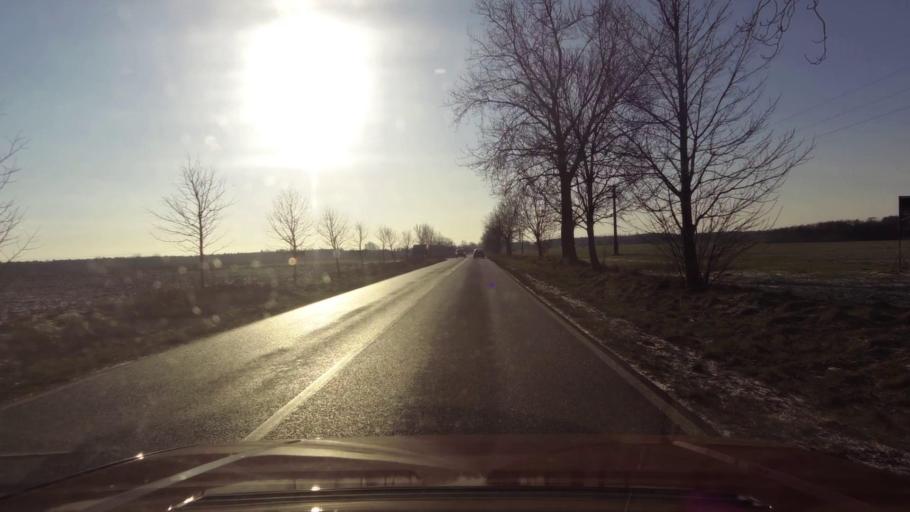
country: PL
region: West Pomeranian Voivodeship
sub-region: Powiat bialogardzki
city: Bialogard
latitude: 54.0405
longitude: 15.9592
